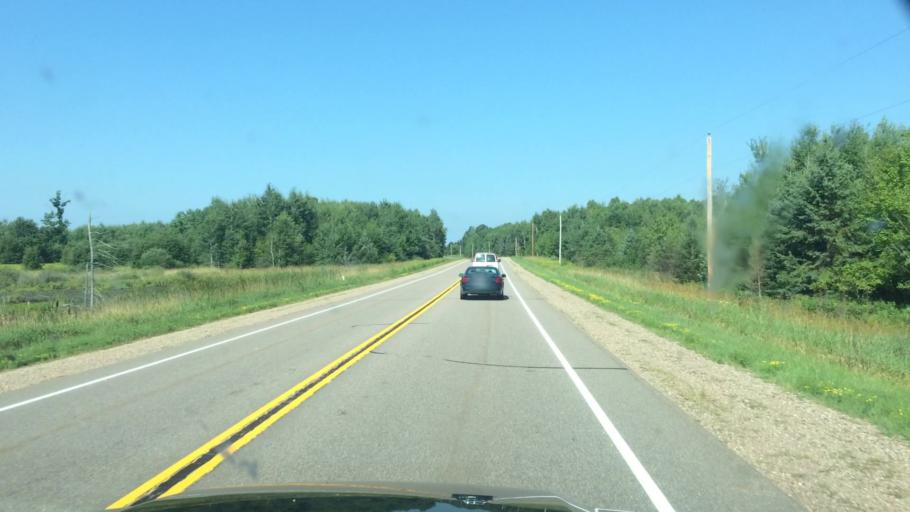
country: US
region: Wisconsin
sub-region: Langlade County
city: Antigo
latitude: 45.1481
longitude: -89.4141
